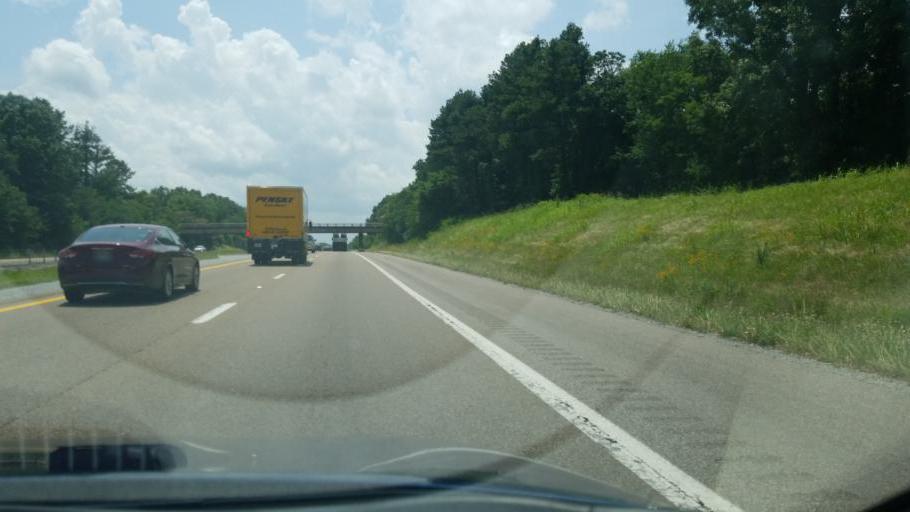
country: US
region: Tennessee
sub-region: Crockett County
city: Bells
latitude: 35.6234
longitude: -88.9809
